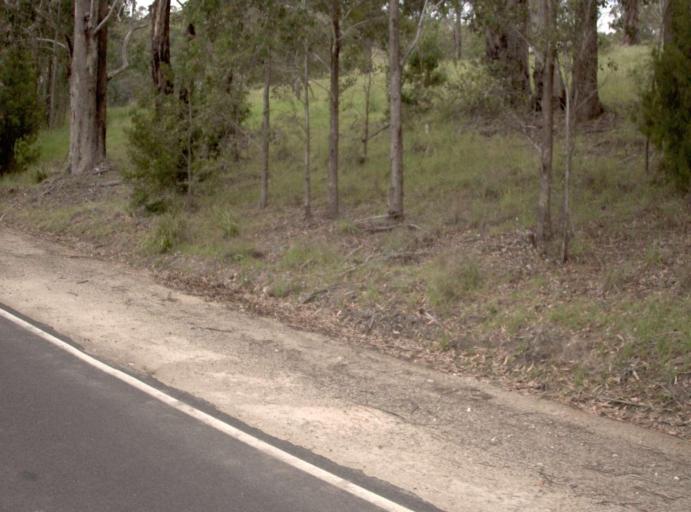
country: AU
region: New South Wales
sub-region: Bombala
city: Bombala
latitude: -37.4562
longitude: 149.1900
